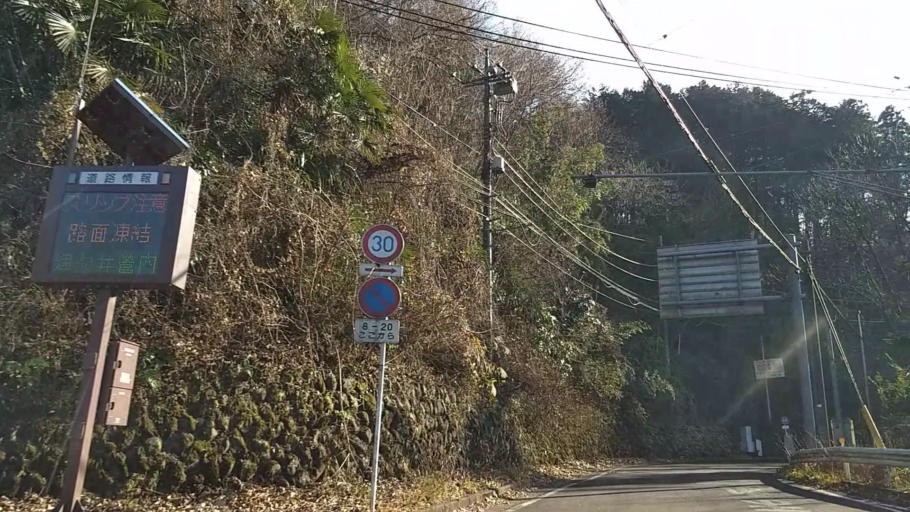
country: JP
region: Yamanashi
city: Uenohara
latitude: 35.5626
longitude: 139.2073
